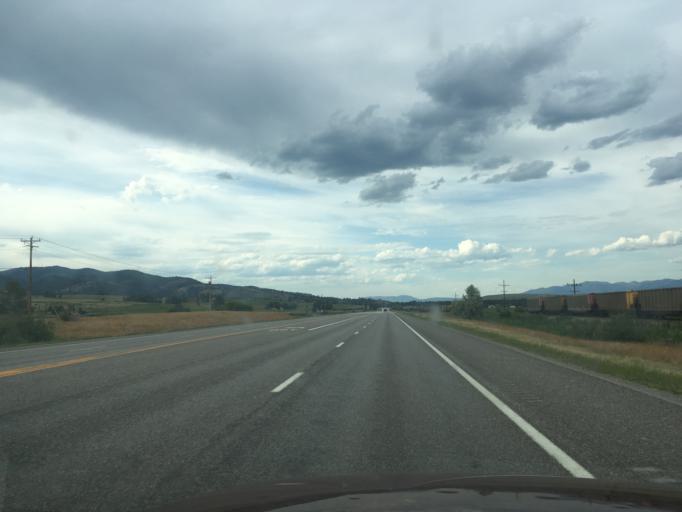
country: US
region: Montana
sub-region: Missoula County
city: Lolo
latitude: 46.7253
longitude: -114.0784
